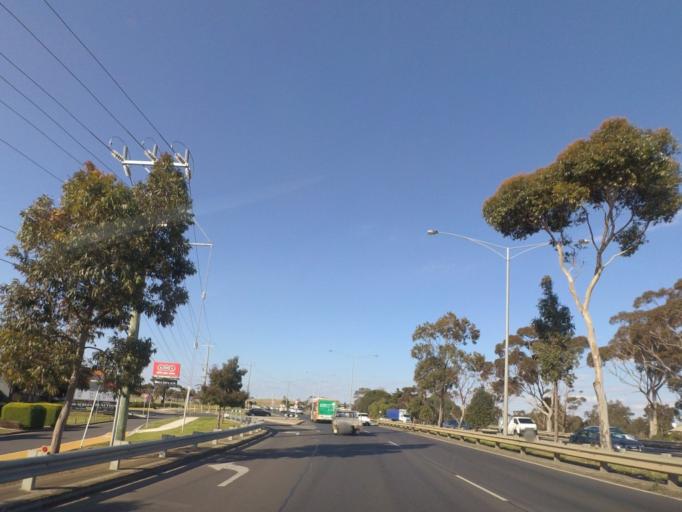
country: AU
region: Victoria
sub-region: Brimbank
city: Deer Park
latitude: -37.7715
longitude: 144.7876
